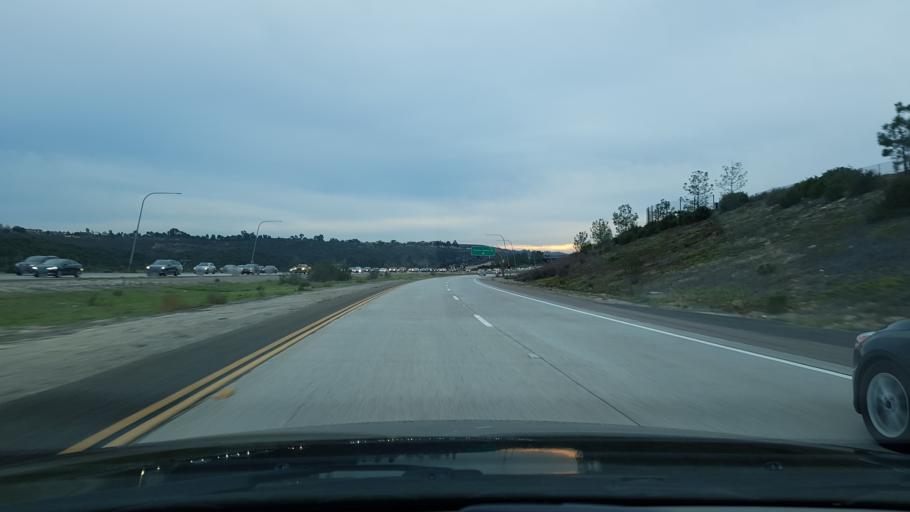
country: US
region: California
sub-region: San Diego County
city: Fairbanks Ranch
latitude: 32.9554
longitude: -117.1874
